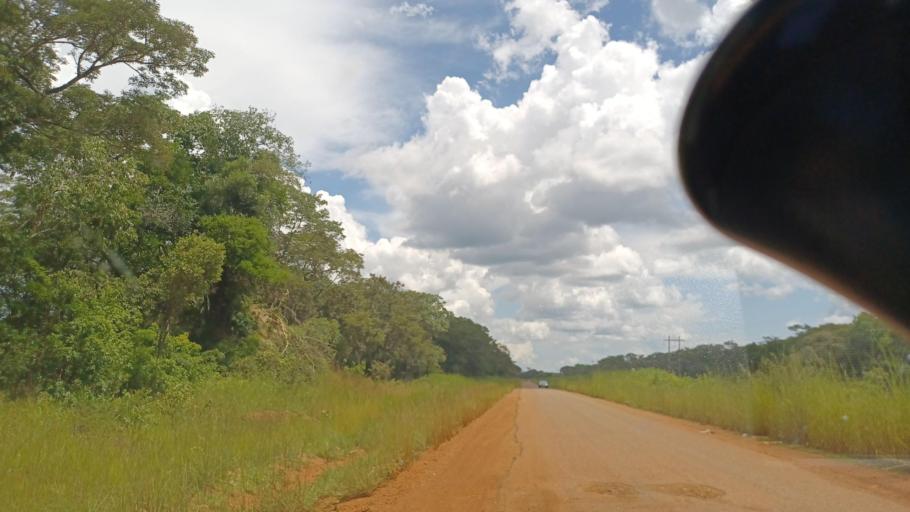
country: ZM
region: North-Western
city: Solwezi
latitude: -12.7108
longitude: 26.0264
